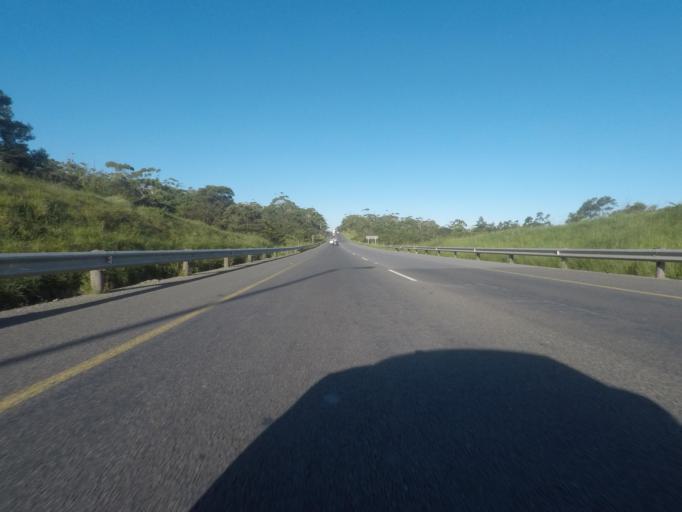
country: ZA
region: Eastern Cape
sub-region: Buffalo City Metropolitan Municipality
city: East London
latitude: -33.0478
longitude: 27.8201
